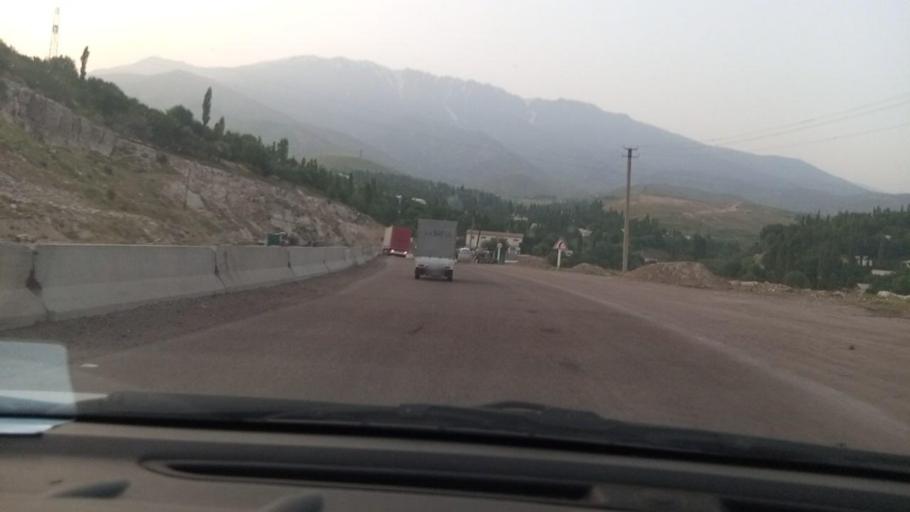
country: UZ
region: Toshkent
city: Angren
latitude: 41.0723
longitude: 70.2520
